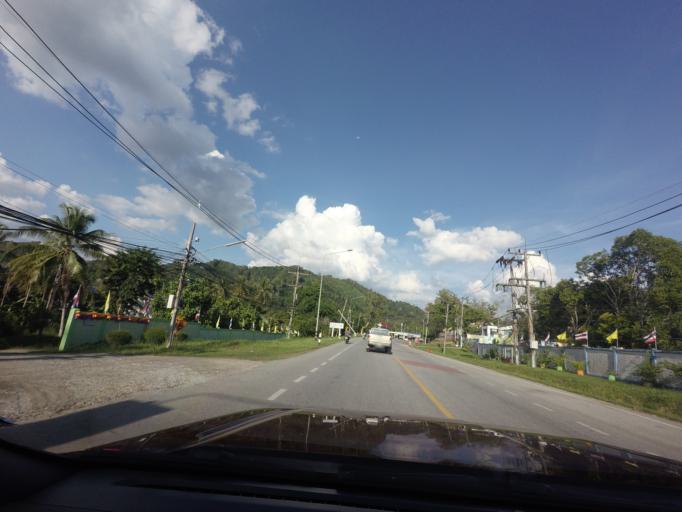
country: TH
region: Yala
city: Than To
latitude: 6.1613
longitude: 101.1866
